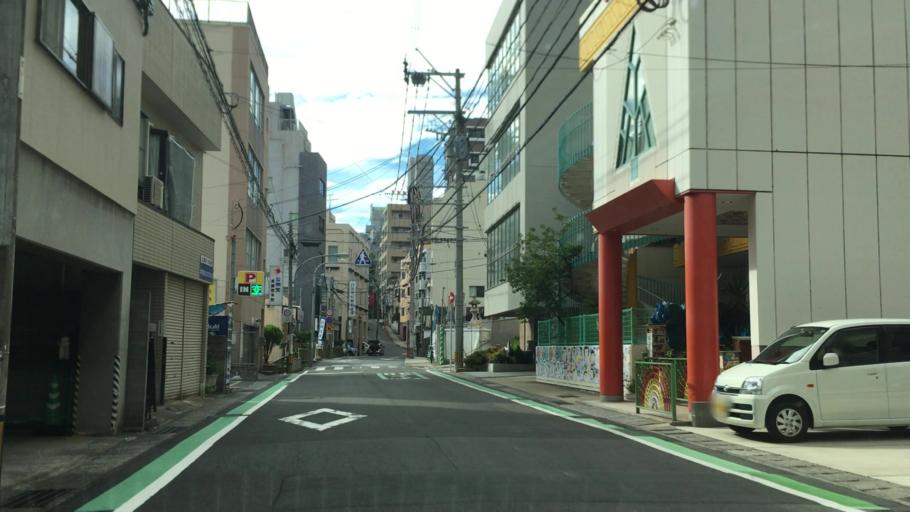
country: JP
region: Nagasaki
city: Nagasaki-shi
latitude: 32.7529
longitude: 129.8736
